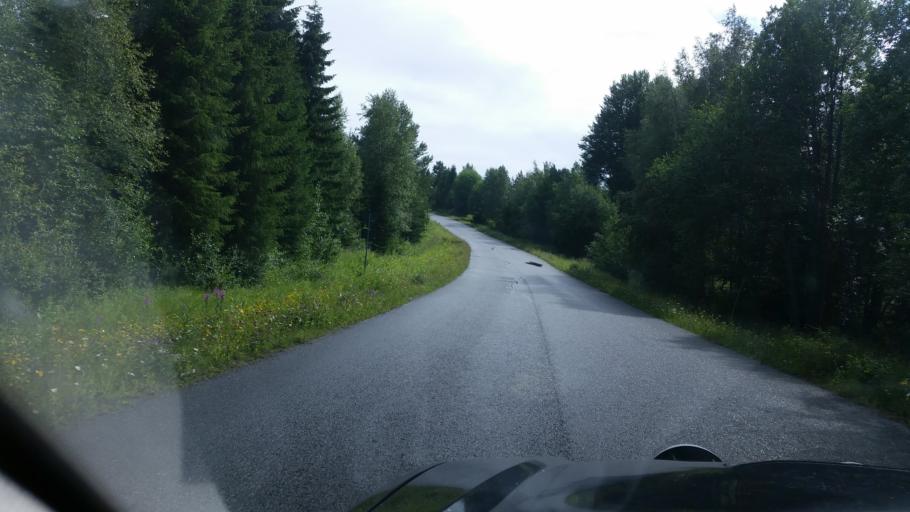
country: SE
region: Jaemtland
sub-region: Krokoms Kommun
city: Krokom
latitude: 63.3234
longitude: 14.3023
